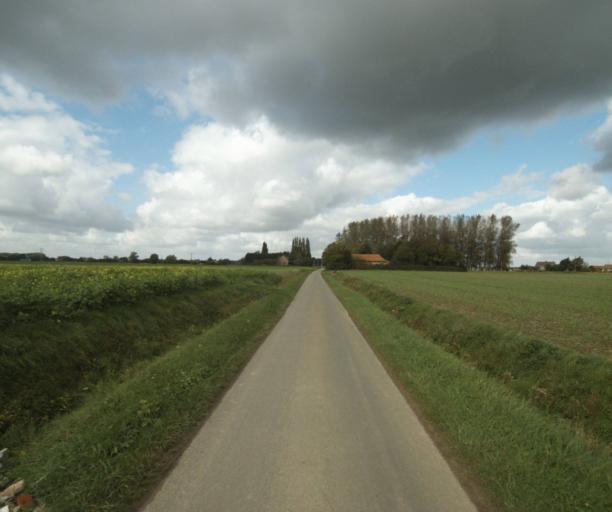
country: FR
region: Nord-Pas-de-Calais
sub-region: Departement du Nord
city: Frelinghien
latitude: 50.7051
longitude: 2.9486
